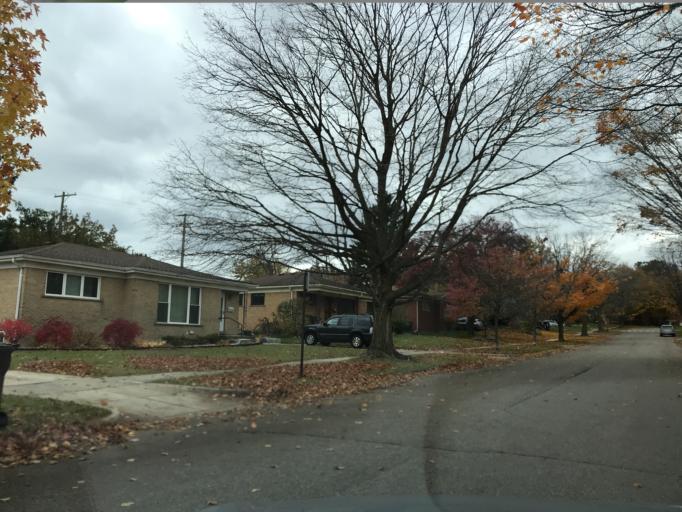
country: US
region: Michigan
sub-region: Washtenaw County
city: Ann Arbor
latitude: 42.2526
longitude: -83.7108
